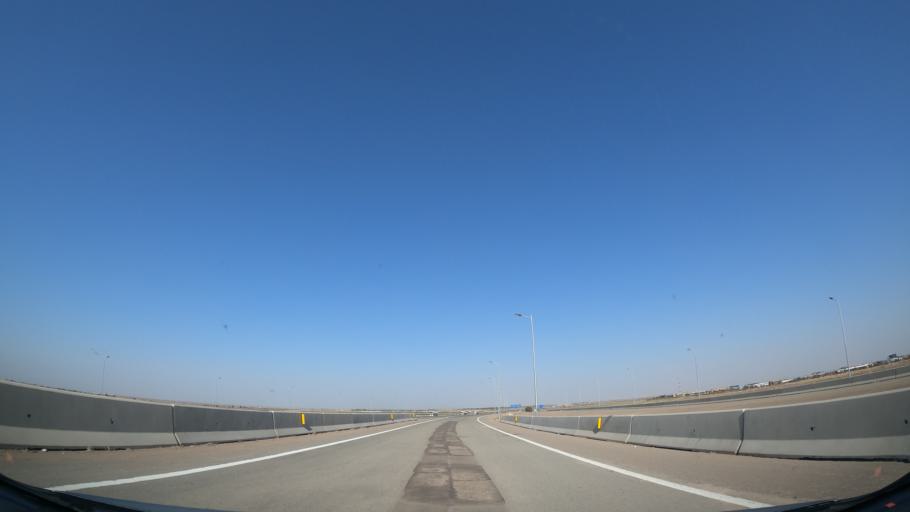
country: IR
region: Tehran
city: Eqbaliyeh
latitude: 35.1368
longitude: 51.5212
